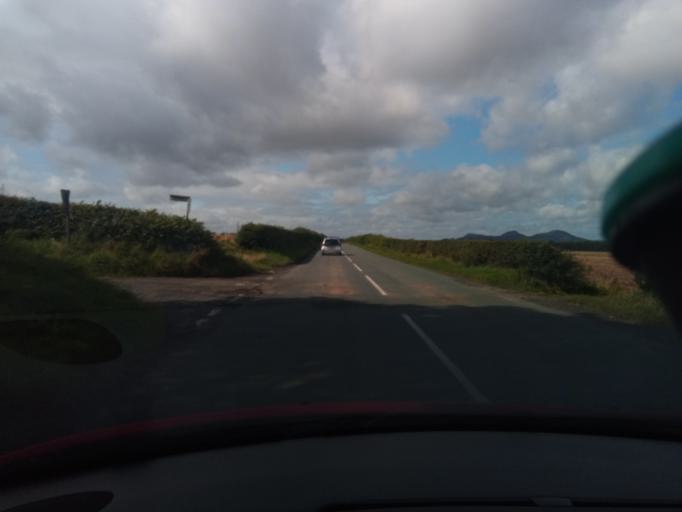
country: GB
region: Scotland
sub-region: The Scottish Borders
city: Saint Boswells
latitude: 55.5719
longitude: -2.5708
